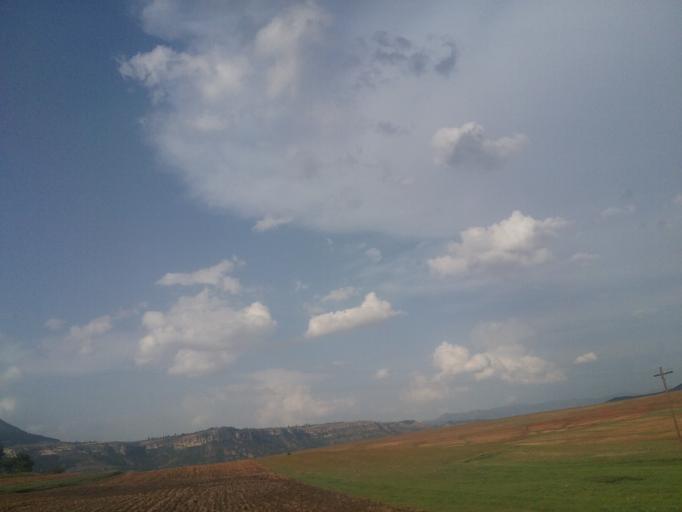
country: LS
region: Leribe
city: Leribe
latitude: -28.9275
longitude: 28.1324
